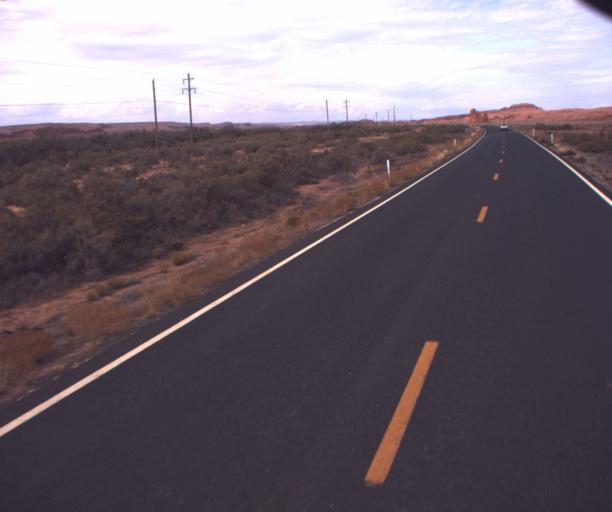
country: US
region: Arizona
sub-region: Apache County
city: Many Farms
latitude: 36.7346
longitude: -109.6335
